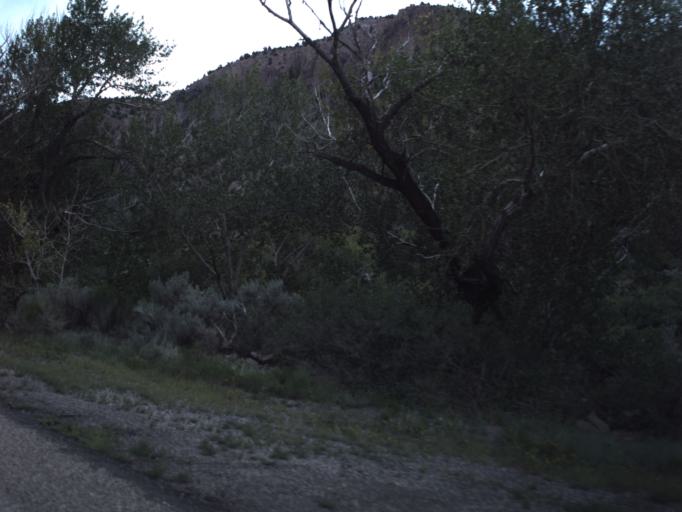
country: US
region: Utah
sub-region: Piute County
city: Junction
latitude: 38.1930
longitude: -112.1063
